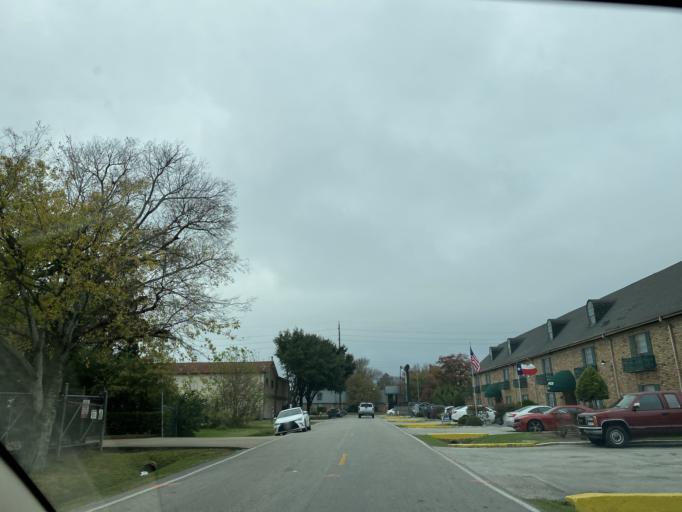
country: US
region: Texas
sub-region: Harris County
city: Bellaire
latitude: 29.7302
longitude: -95.4828
